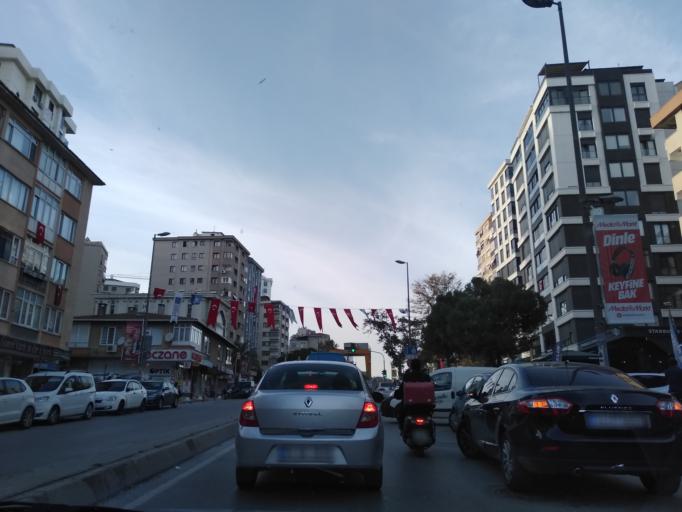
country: TR
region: Istanbul
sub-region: Atasehir
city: Atasehir
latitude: 40.9652
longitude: 29.0880
